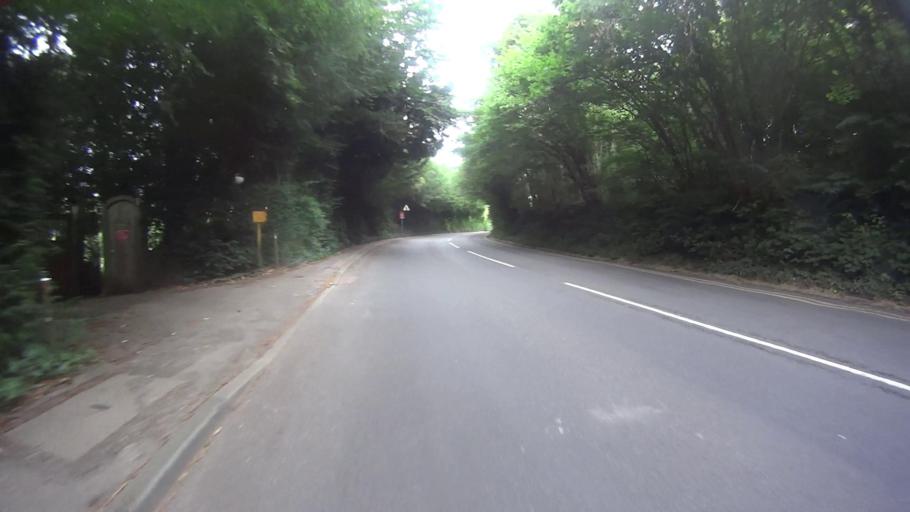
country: GB
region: England
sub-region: Surrey
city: Mickleham
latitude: 51.2567
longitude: -0.3228
